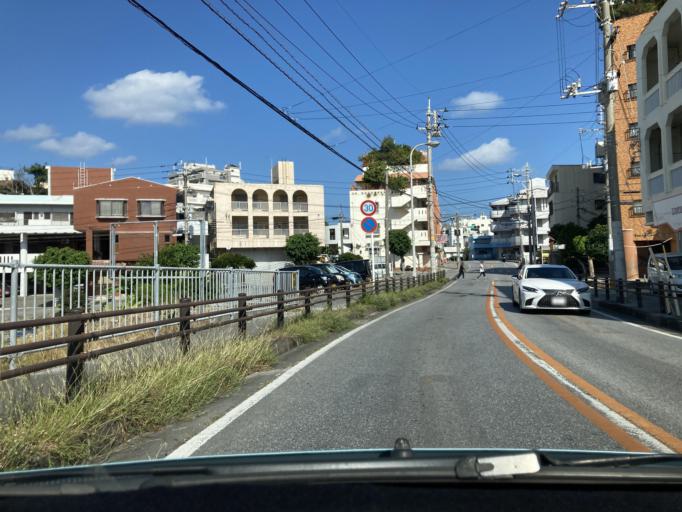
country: JP
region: Okinawa
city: Tomigusuku
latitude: 26.1838
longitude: 127.6609
